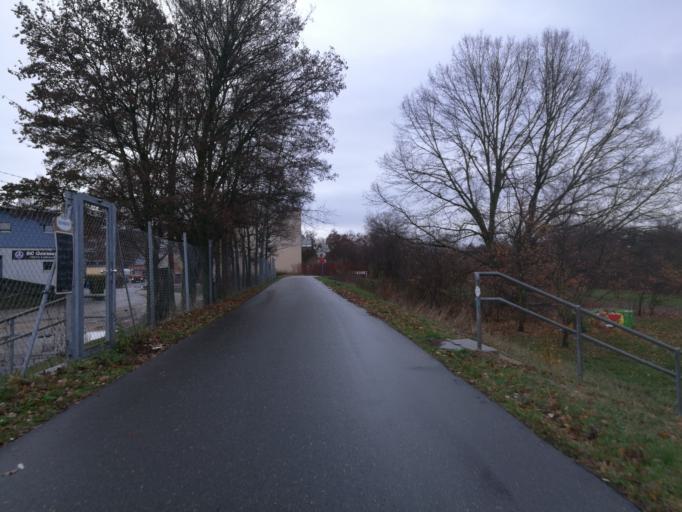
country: DE
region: Bavaria
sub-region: Regierungsbezirk Mittelfranken
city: Wetzendorf
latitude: 49.4672
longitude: 11.0234
